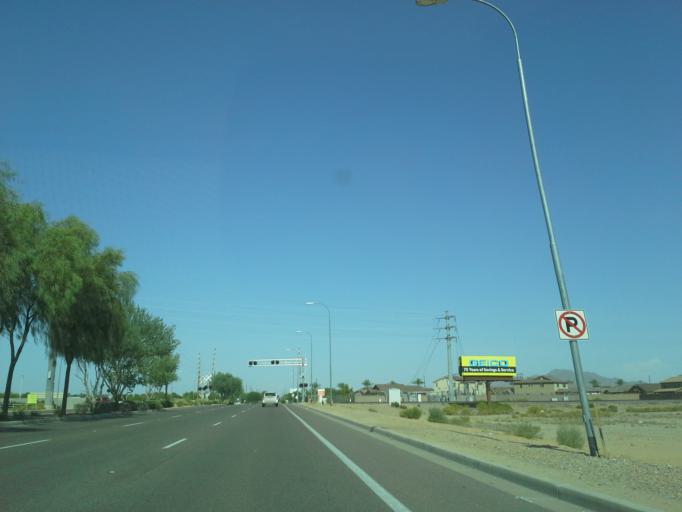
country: US
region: Arizona
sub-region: Maricopa County
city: Sun Lakes
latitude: 33.2185
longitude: -111.8380
